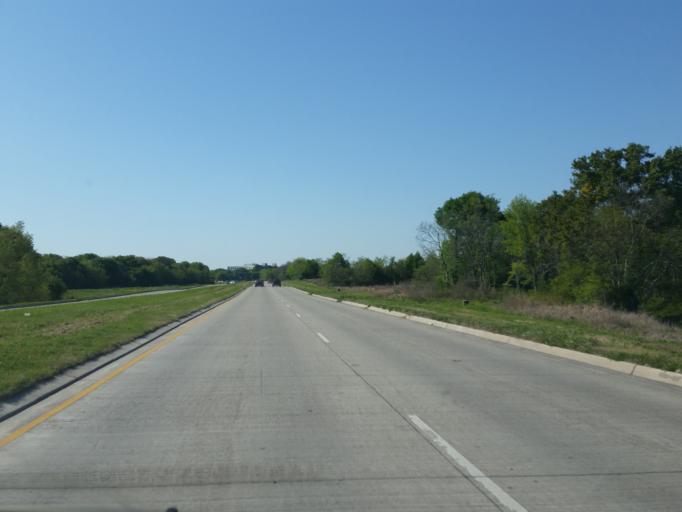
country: US
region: Louisiana
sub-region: Lafayette Parish
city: Youngsville
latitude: 30.1415
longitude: -92.0252
